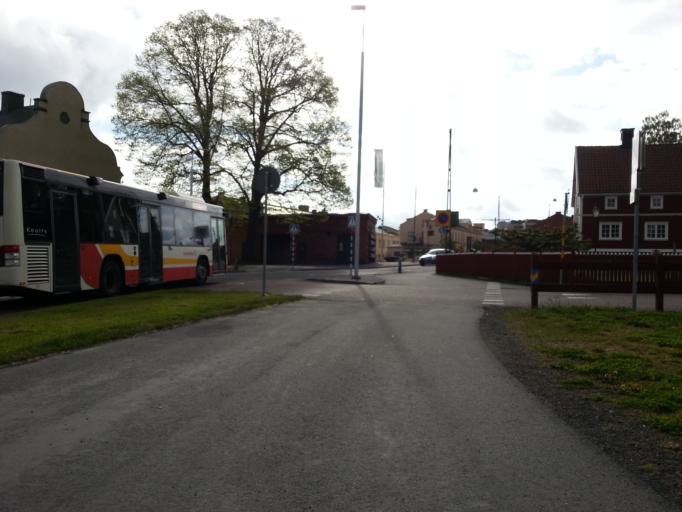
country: SE
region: Joenkoeping
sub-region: Jonkopings Kommun
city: Jonkoping
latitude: 57.7853
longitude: 14.1546
